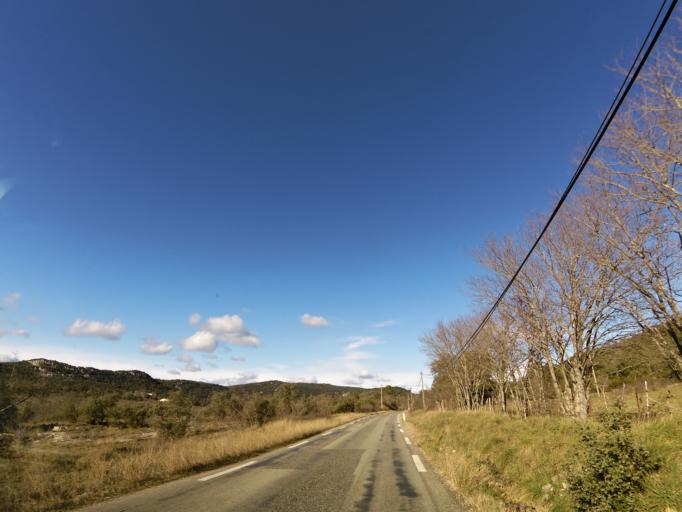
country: FR
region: Languedoc-Roussillon
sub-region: Departement du Gard
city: Sauve
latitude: 43.9599
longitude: 3.9461
